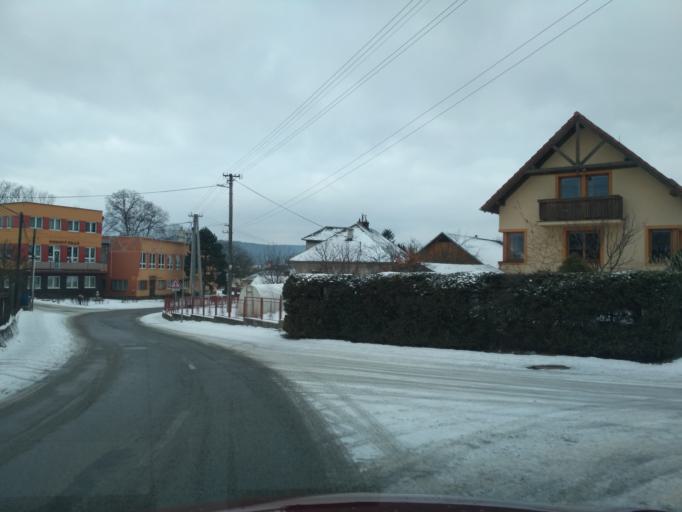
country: SK
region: Presovsky
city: Sabinov
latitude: 49.0100
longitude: 21.1261
